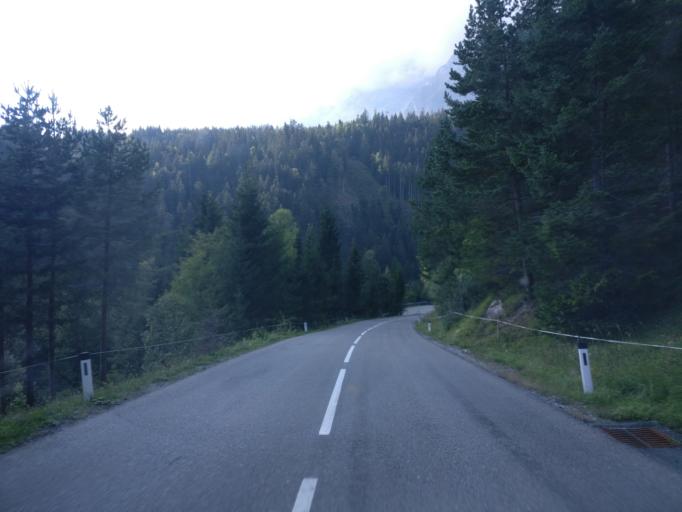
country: AT
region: Salzburg
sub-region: Politischer Bezirk Sankt Johann im Pongau
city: Muhlbach am Hochkonig
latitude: 47.3896
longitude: 13.1128
